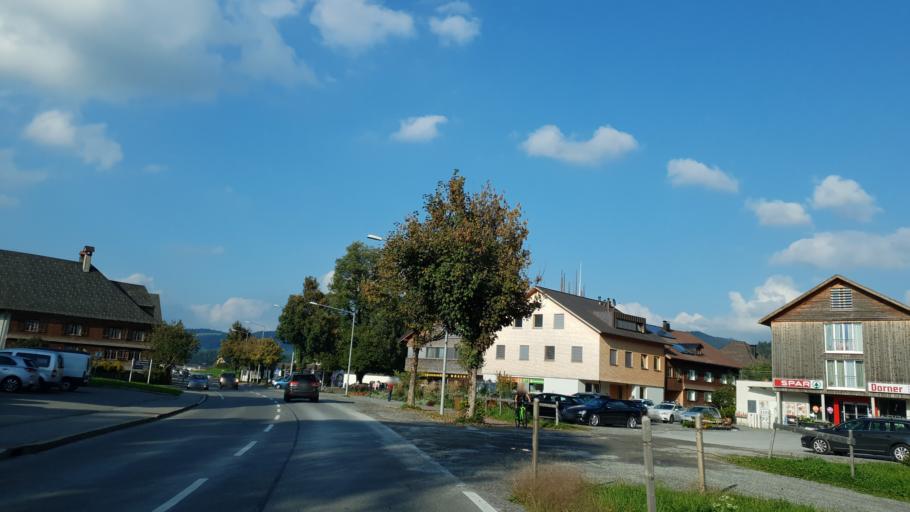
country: AT
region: Vorarlberg
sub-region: Politischer Bezirk Bregenz
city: Andelsbuch
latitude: 47.4125
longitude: 9.8946
